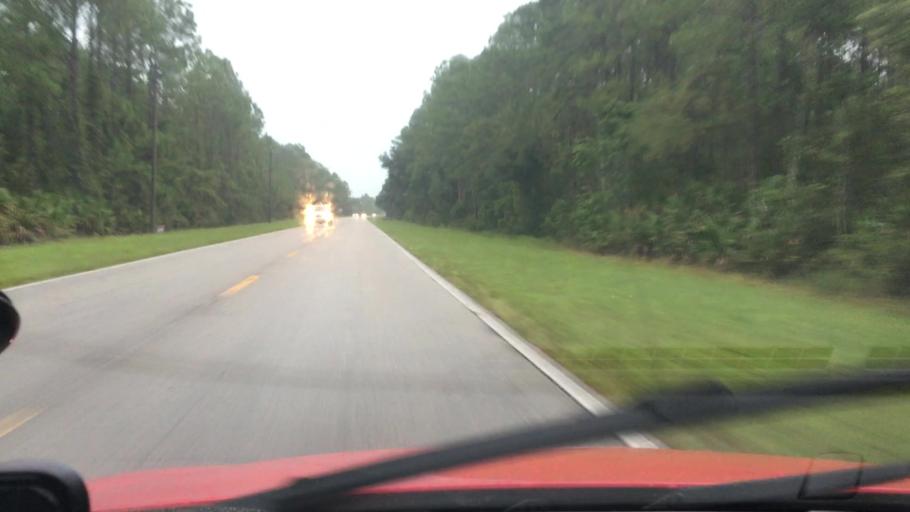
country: US
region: Florida
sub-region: Volusia County
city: Samsula-Spruce Creek
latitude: 29.0393
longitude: -81.0804
